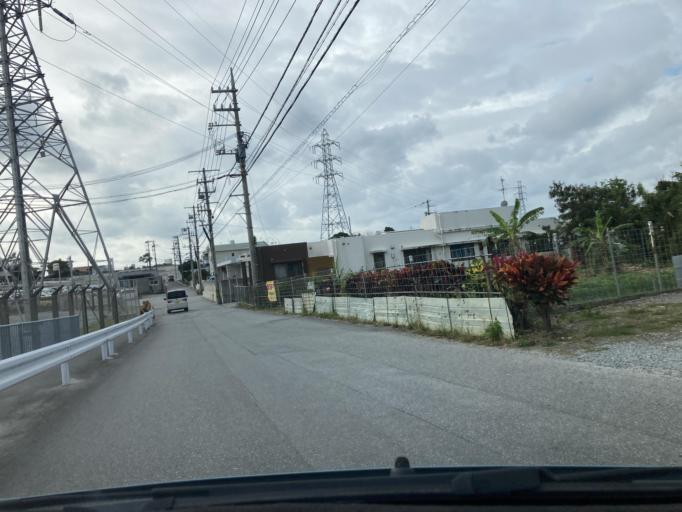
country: JP
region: Okinawa
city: Ginowan
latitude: 26.2045
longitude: 127.7470
